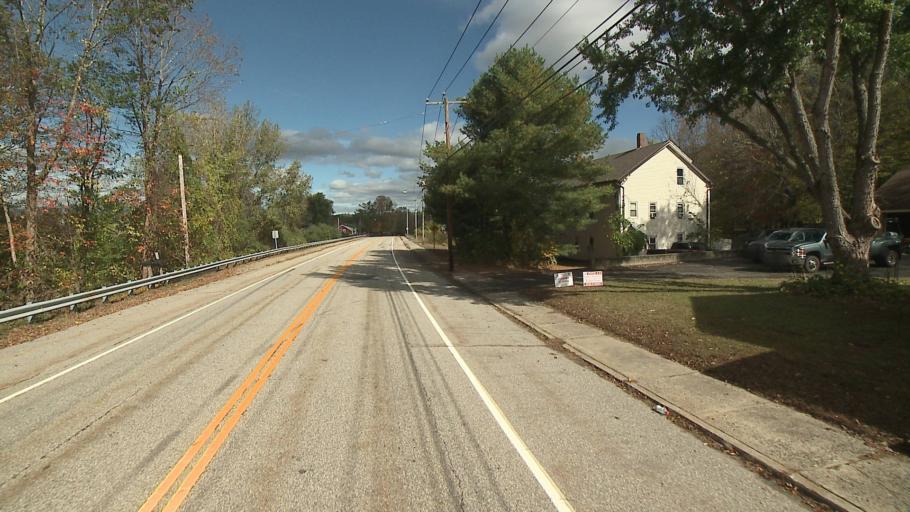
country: US
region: Connecticut
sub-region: Windham County
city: Putnam
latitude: 41.9390
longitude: -71.8945
